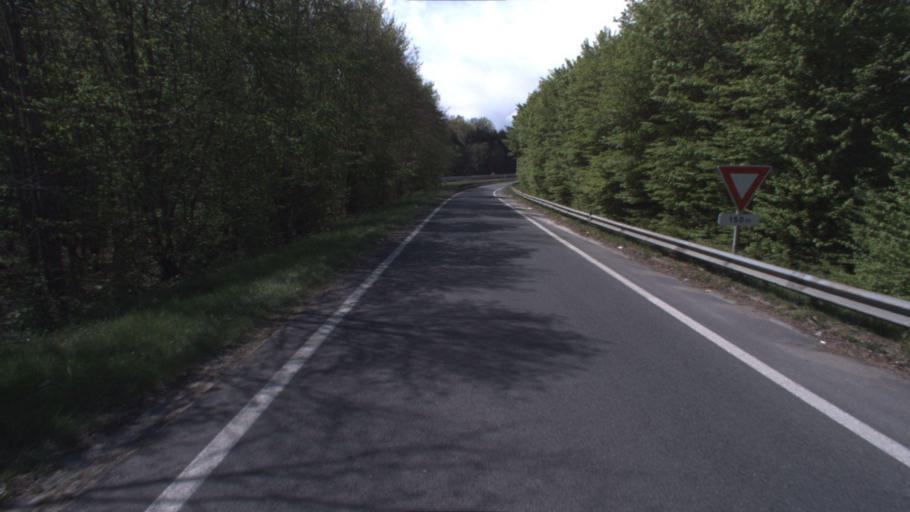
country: FR
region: Ile-de-France
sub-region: Departement de Seine-et-Marne
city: Fontenay-Tresigny
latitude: 48.7196
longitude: 2.8469
